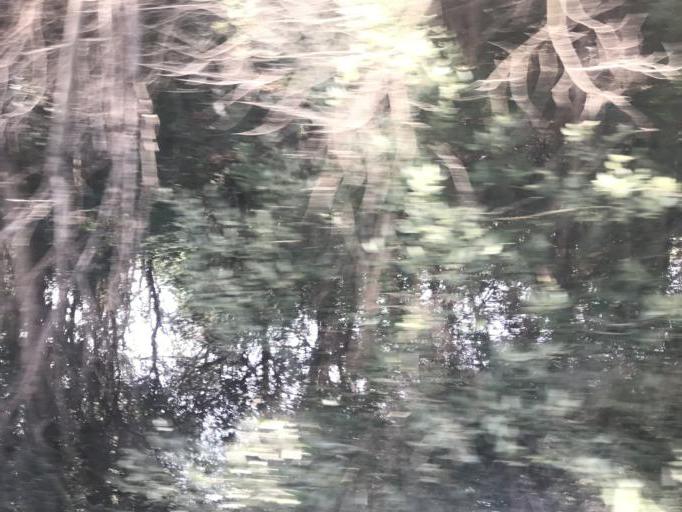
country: AR
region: Cordoba
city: Laguna Larga
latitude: -31.7971
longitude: -63.7855
